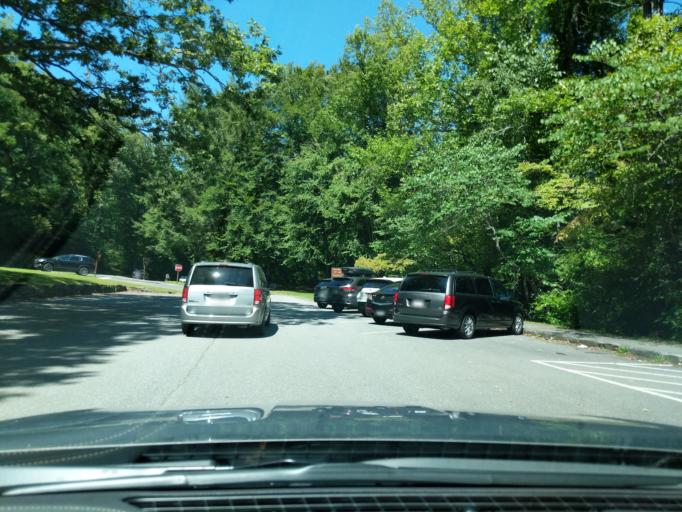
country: US
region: North Carolina
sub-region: Swain County
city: Cherokee
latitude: 35.5141
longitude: -83.3066
